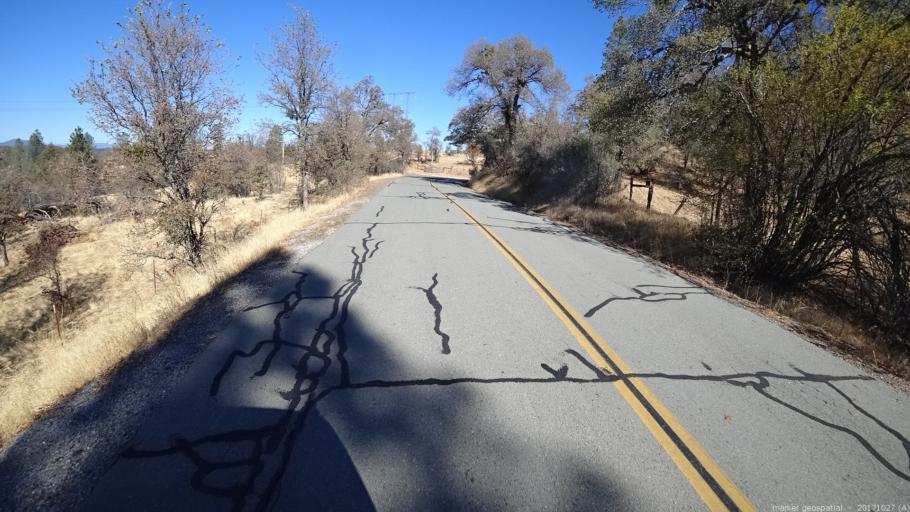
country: US
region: California
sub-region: Shasta County
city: Shingletown
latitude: 40.7562
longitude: -121.9671
